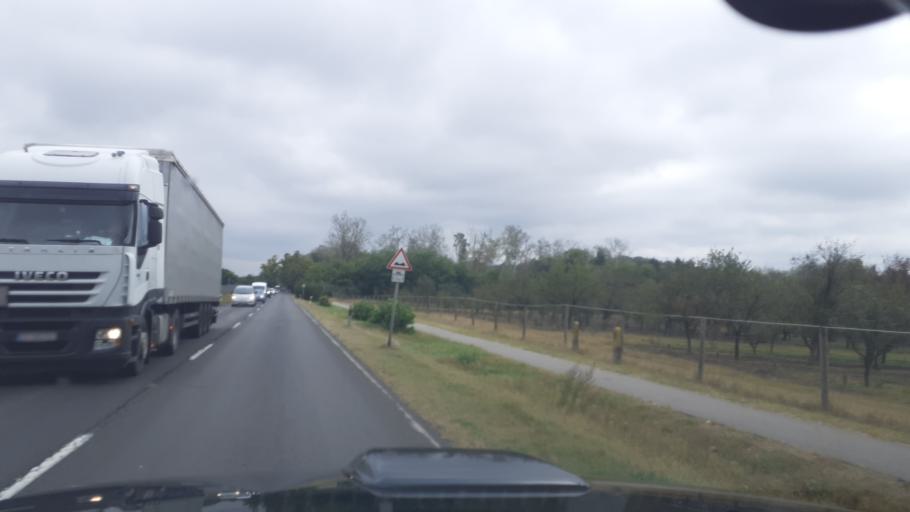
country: HU
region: Bacs-Kiskun
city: Balloszog
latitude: 46.8884
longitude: 19.5908
